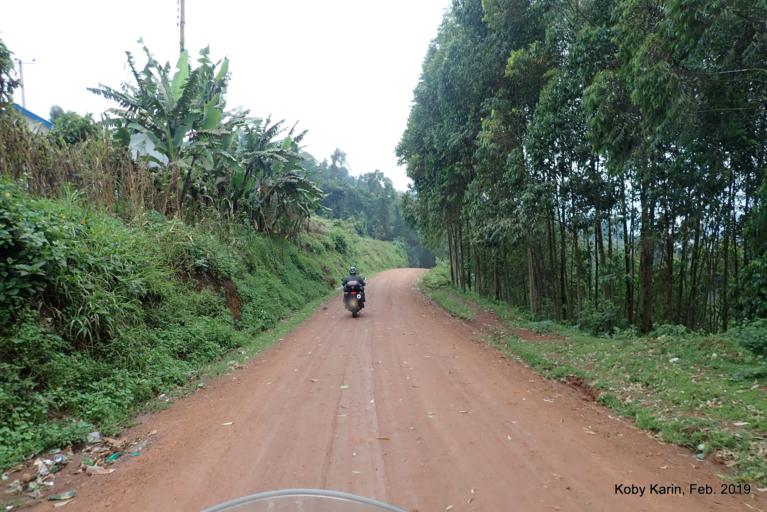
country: UG
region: Western Region
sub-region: Kabale District
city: Kabale
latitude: -1.2585
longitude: 29.9447
